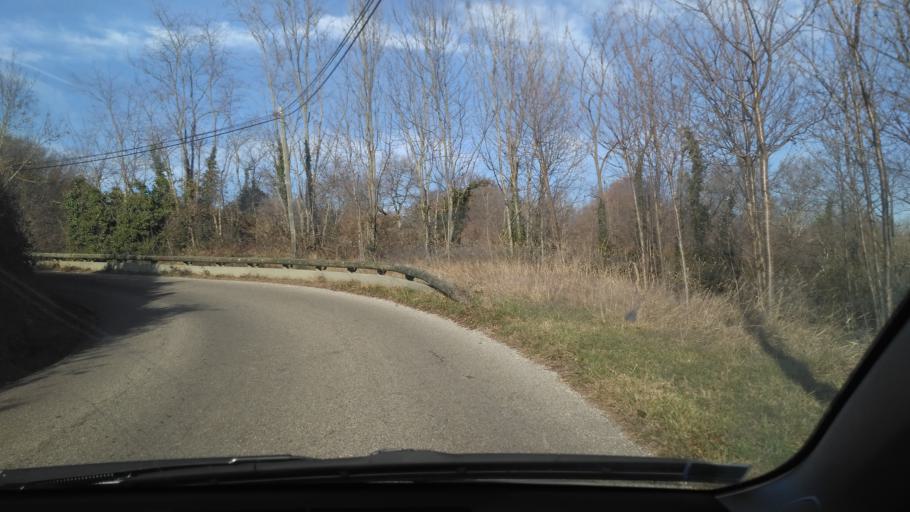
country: FR
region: Rhone-Alpes
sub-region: Departement de l'Isere
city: Saint-Antoine-l'Abbaye
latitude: 45.1786
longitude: 5.2118
